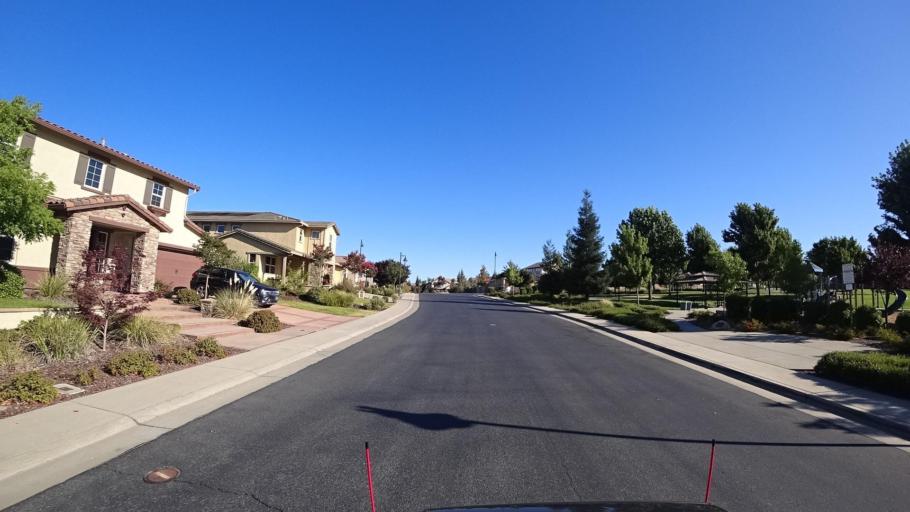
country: US
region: California
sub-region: Placer County
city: Rocklin
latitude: 38.8269
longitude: -121.2767
